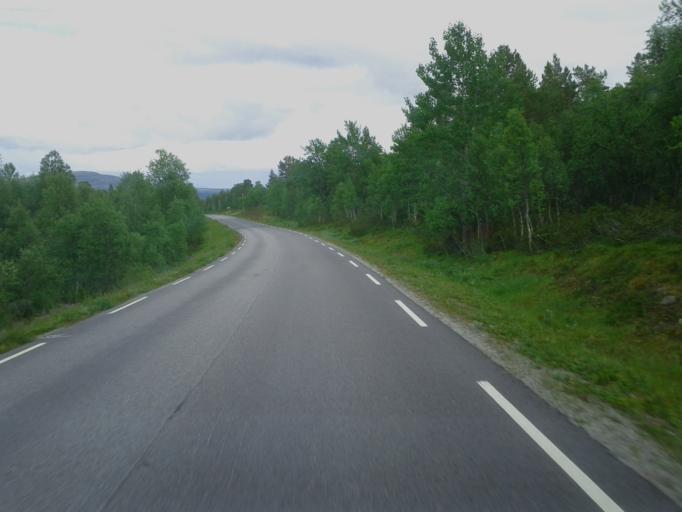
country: NO
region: Sor-Trondelag
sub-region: Roros
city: Roros
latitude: 62.3153
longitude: 11.6461
